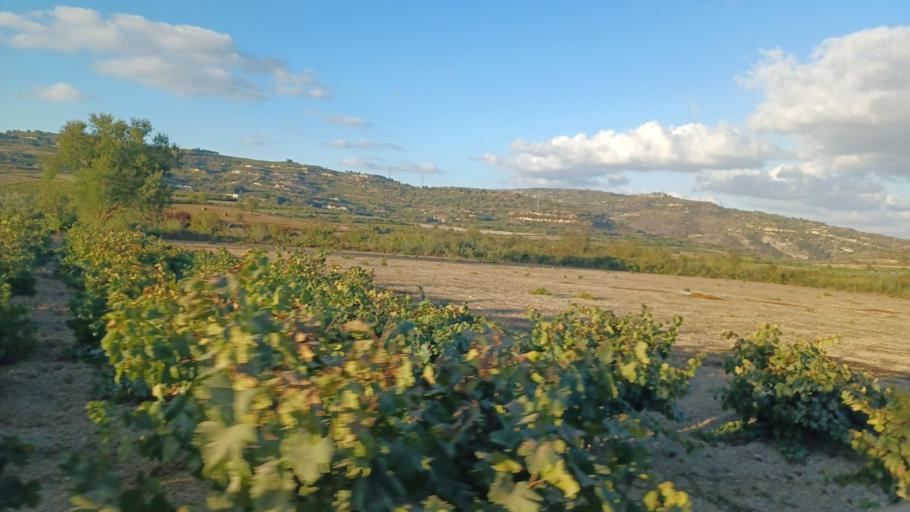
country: CY
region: Pafos
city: Mesogi
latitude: 34.8725
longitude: 32.5009
